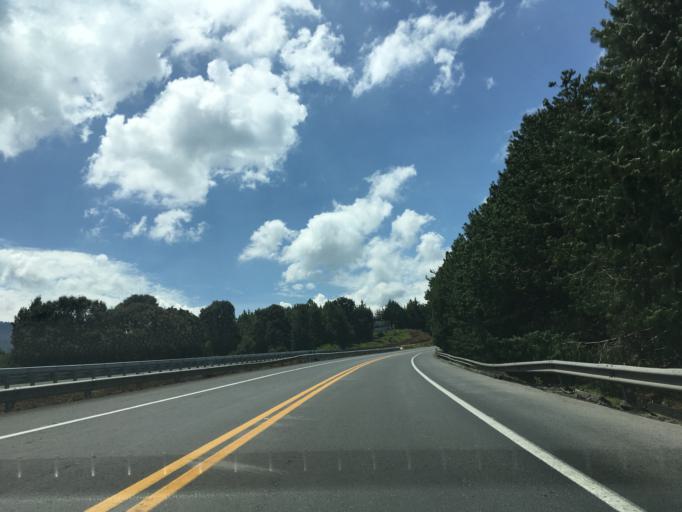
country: MX
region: Michoacan
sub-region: Patzcuaro
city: Colonia Vista Bella (Lomas del Peaje)
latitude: 19.5108
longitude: -101.5738
